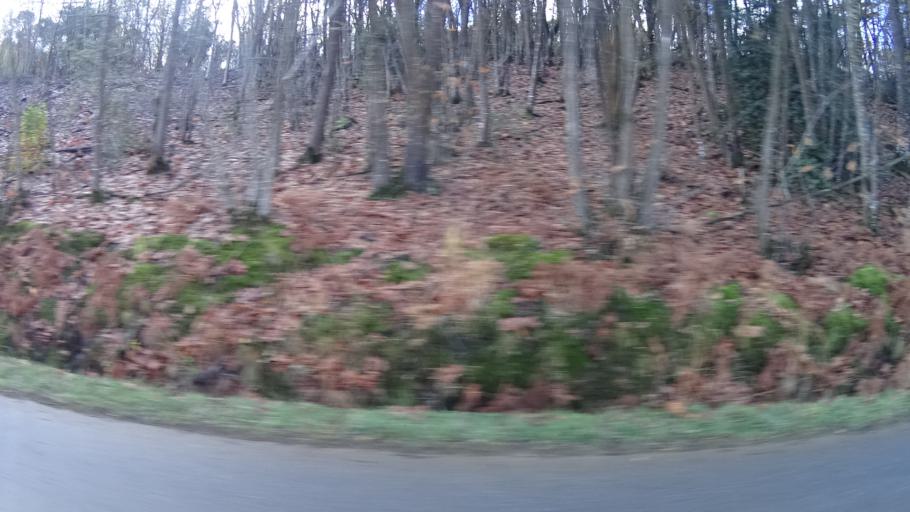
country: FR
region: Brittany
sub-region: Departement du Morbihan
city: Saint-Jean-la-Poterie
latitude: 47.6377
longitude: -2.1097
